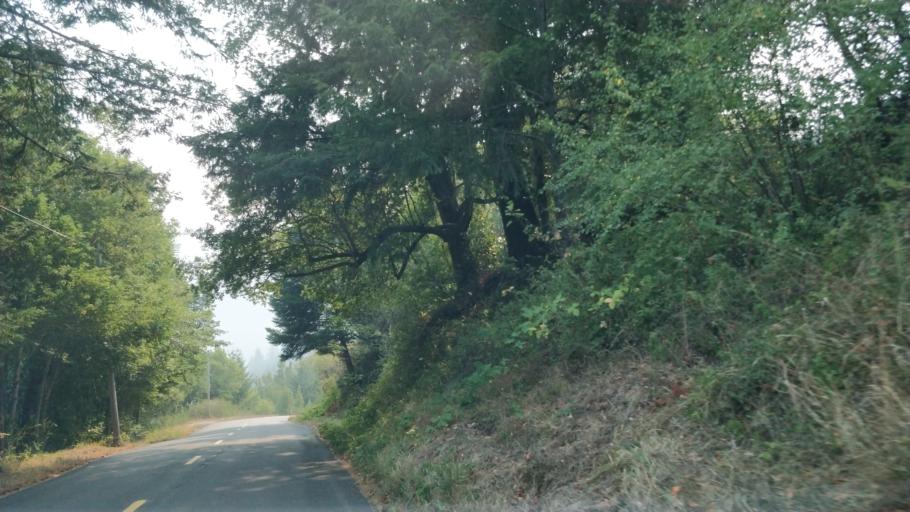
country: US
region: California
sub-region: Humboldt County
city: Rio Dell
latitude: 40.2922
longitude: -124.2515
